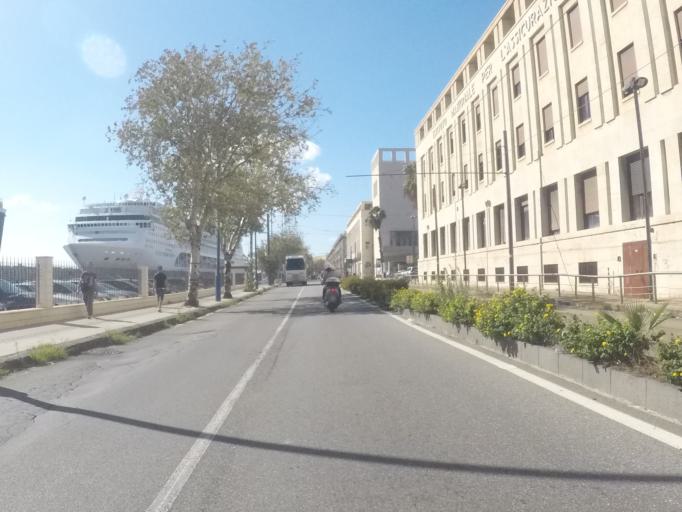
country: IT
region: Sicily
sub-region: Messina
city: Messina
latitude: 38.1947
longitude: 15.5575
